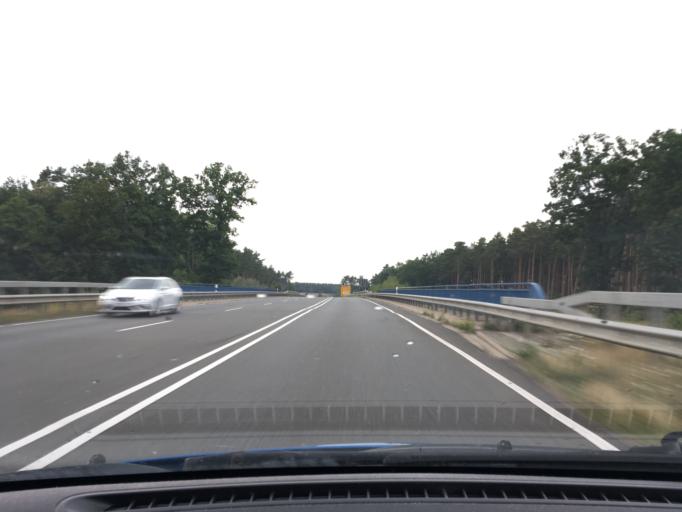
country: DE
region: Lower Saxony
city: Adelheidsdorf
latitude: 52.5760
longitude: 10.0769
